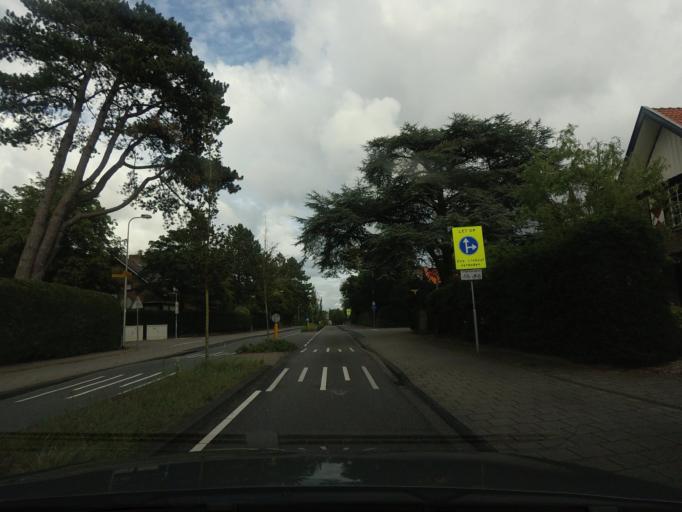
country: NL
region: North Holland
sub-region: Gemeente Bloemendaal
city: Bloemendaal
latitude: 52.3923
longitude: 4.6064
